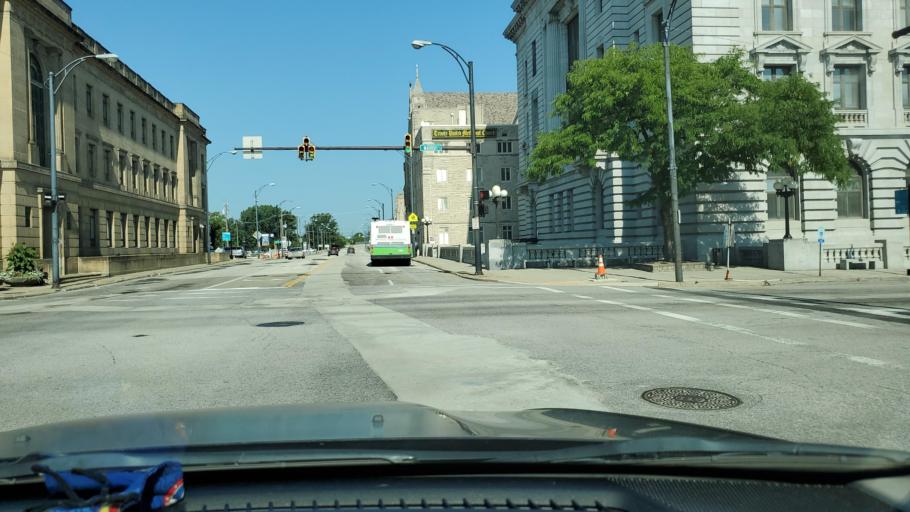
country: US
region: Ohio
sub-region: Mahoning County
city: Youngstown
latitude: 41.0983
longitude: -80.6505
